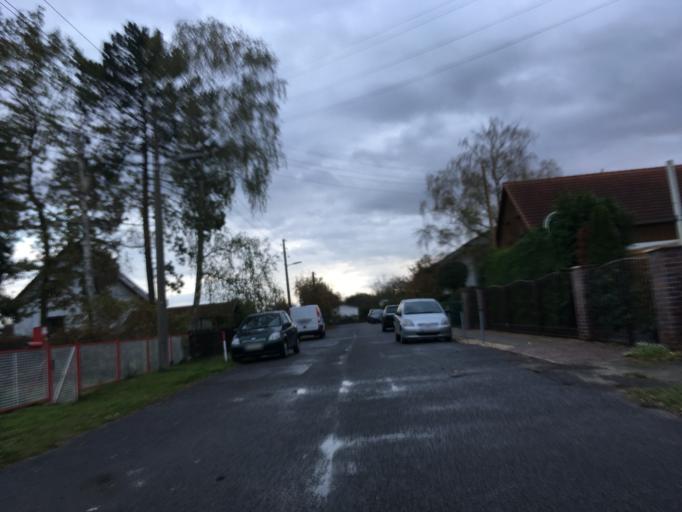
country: DE
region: Berlin
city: Wilhelmsruh
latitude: 52.5890
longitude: 13.3790
